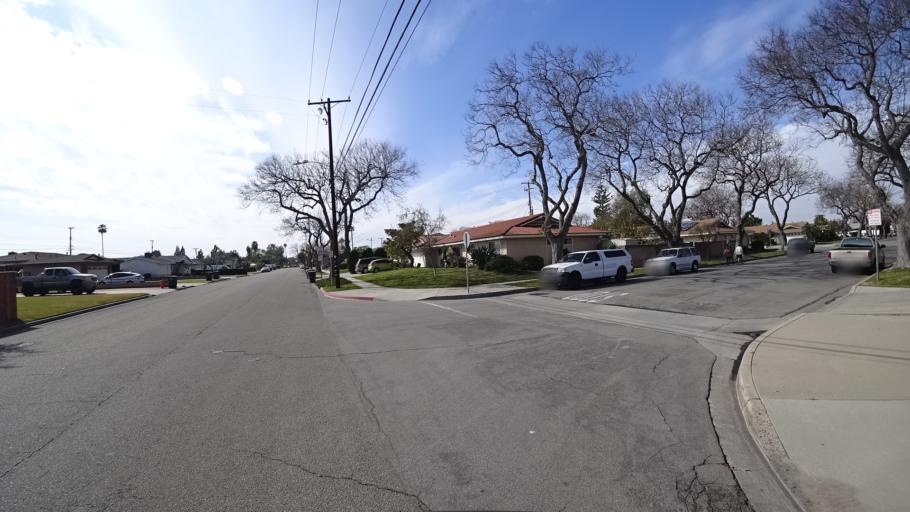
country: US
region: California
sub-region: Orange County
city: Anaheim
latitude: 33.7925
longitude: -117.9001
